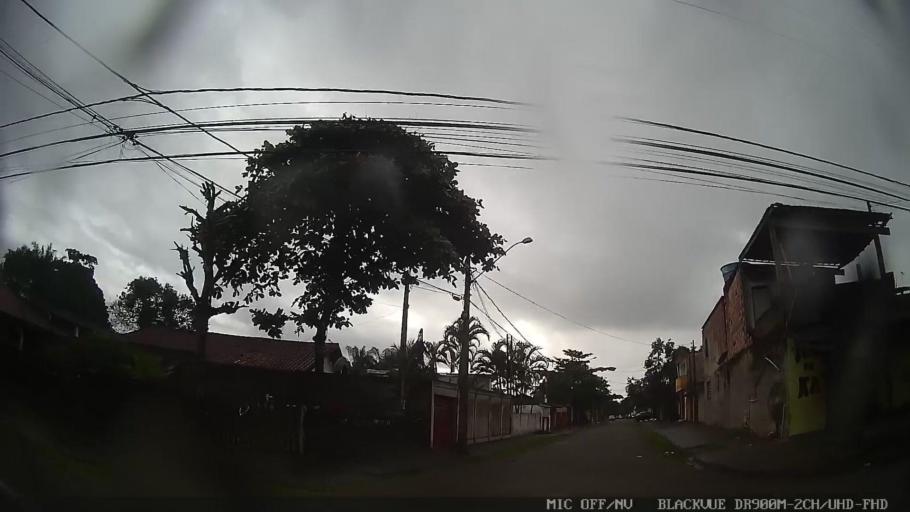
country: BR
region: Sao Paulo
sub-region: Itanhaem
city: Itanhaem
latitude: -24.2340
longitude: -46.8843
